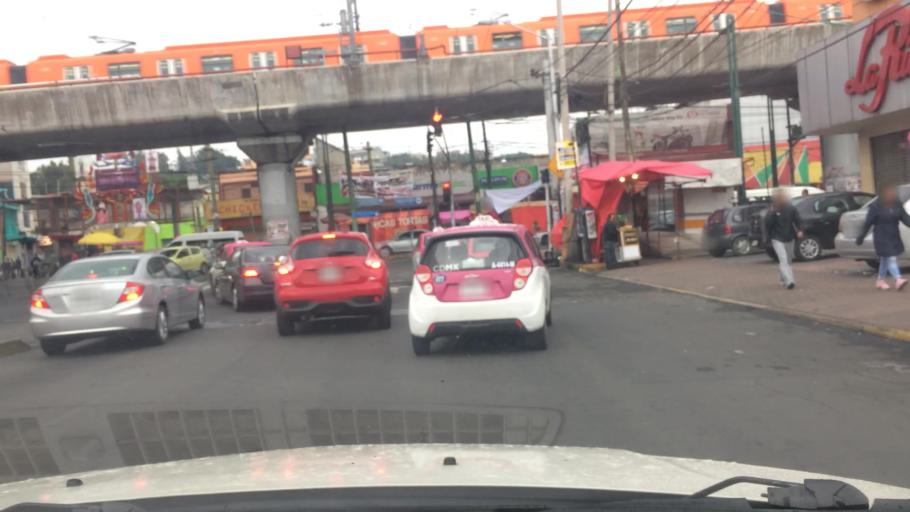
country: MX
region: Mexico City
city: Iztapalapa
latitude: 19.3380
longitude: -99.1093
